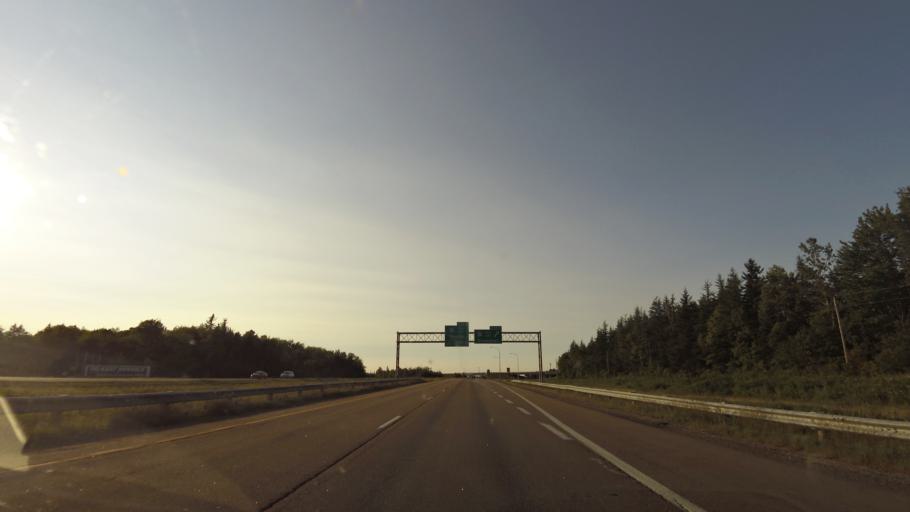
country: CA
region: New Brunswick
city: Dieppe
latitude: 46.0974
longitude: -64.6028
